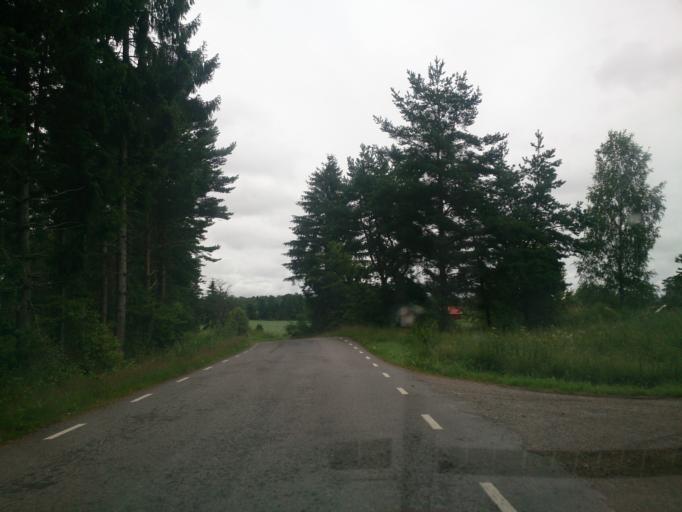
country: SE
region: OEstergoetland
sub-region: Norrkopings Kommun
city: Krokek
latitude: 58.4971
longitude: 16.5498
